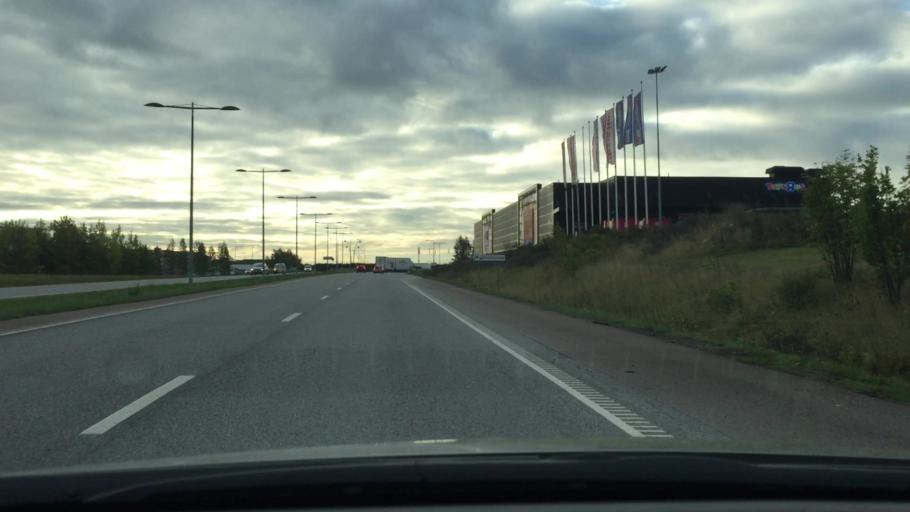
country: SE
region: Uppsala
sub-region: Uppsala Kommun
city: Saevja
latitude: 59.8564
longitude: 17.6819
